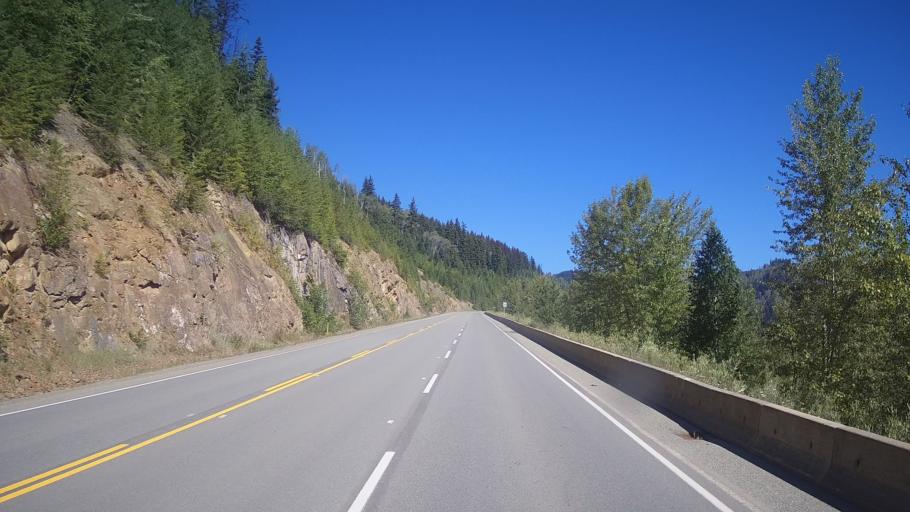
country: CA
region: British Columbia
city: Kamloops
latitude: 51.4825
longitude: -120.2623
